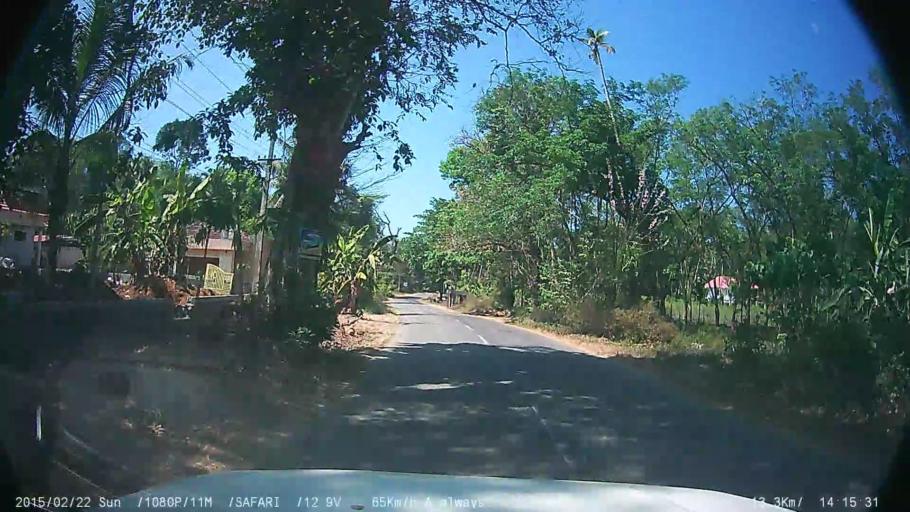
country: IN
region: Kerala
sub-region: Kottayam
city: Kottayam
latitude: 9.5504
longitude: 76.6832
